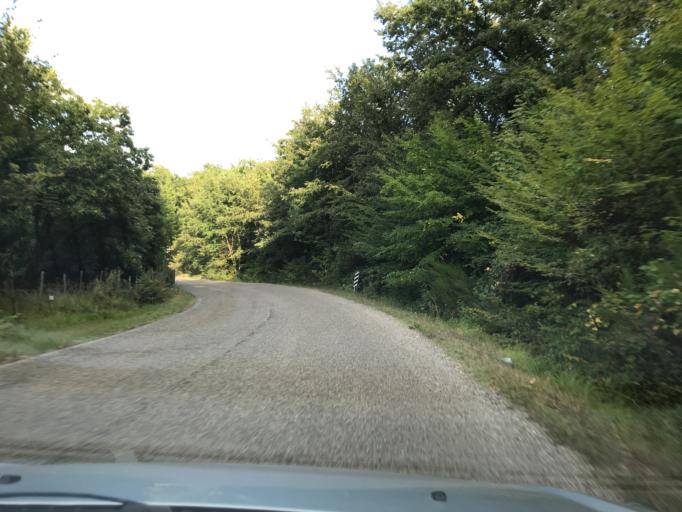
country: IT
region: Umbria
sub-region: Provincia di Terni
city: Guardea
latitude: 42.6470
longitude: 12.3535
